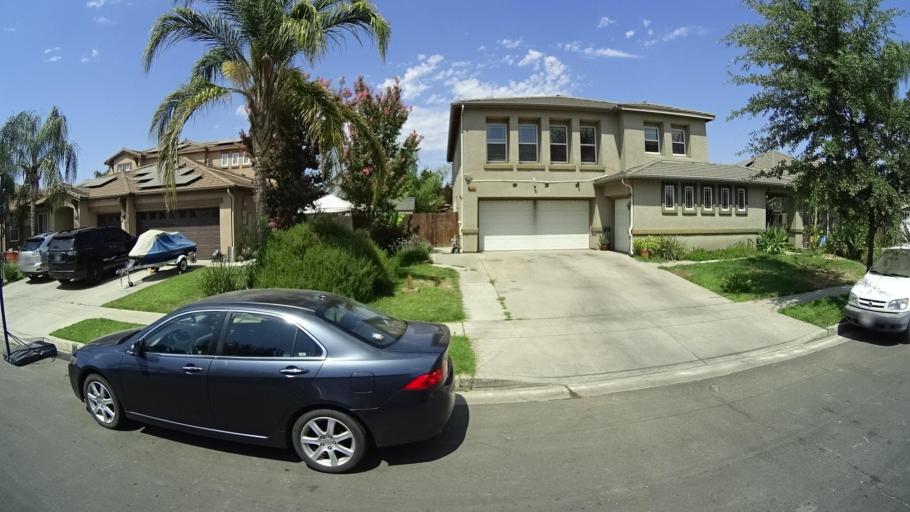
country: US
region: California
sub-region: Fresno County
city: Tarpey Village
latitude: 36.7806
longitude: -119.6763
